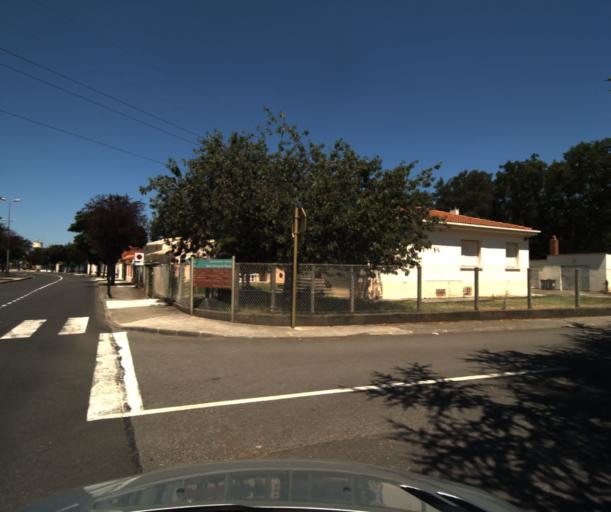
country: FR
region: Midi-Pyrenees
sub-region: Departement de la Haute-Garonne
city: Roquettes
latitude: 43.4942
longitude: 1.3768
